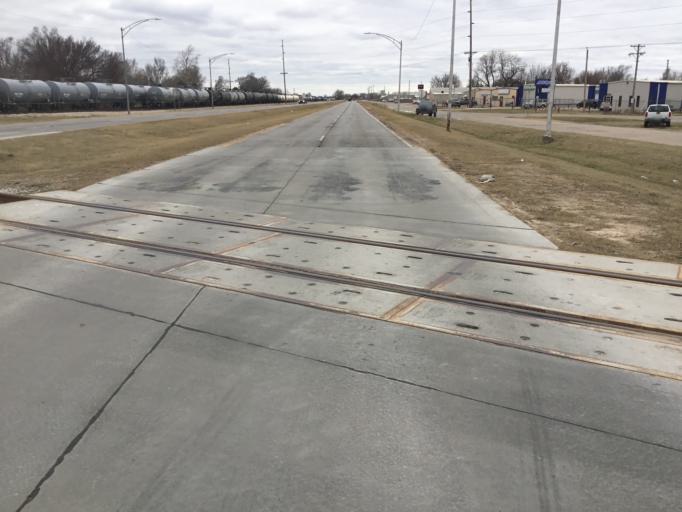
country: US
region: Kansas
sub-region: Sedgwick County
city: Wichita
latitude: 37.6646
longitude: -97.3793
